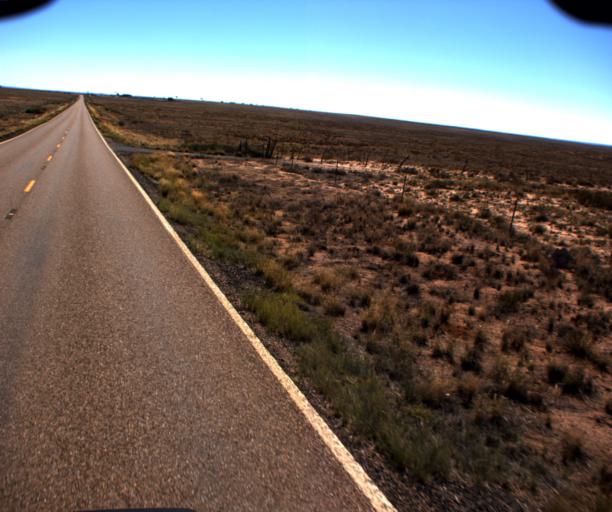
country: US
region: Arizona
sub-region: Navajo County
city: Holbrook
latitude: 34.9967
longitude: -110.0893
